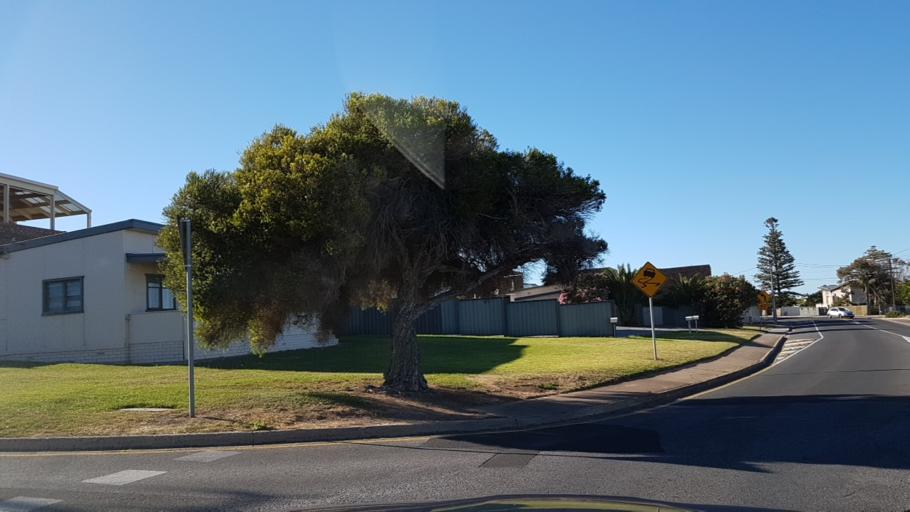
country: AU
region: South Australia
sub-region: Adelaide
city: Port Noarlunga
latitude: -35.1352
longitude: 138.4734
